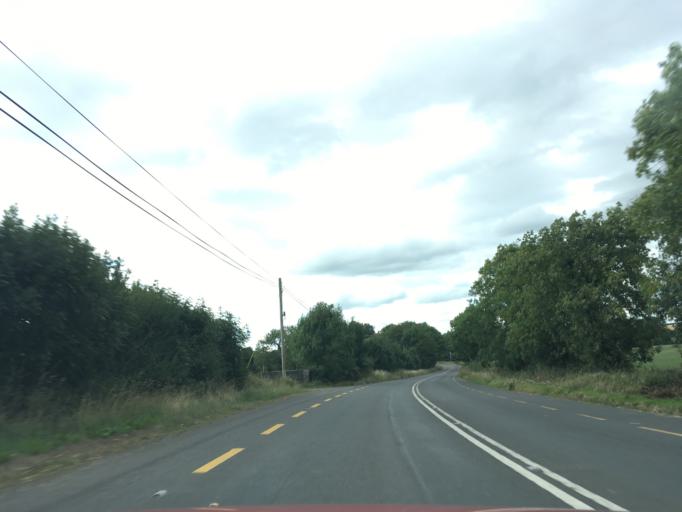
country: IE
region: Munster
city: Cahir
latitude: 52.4233
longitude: -7.8883
